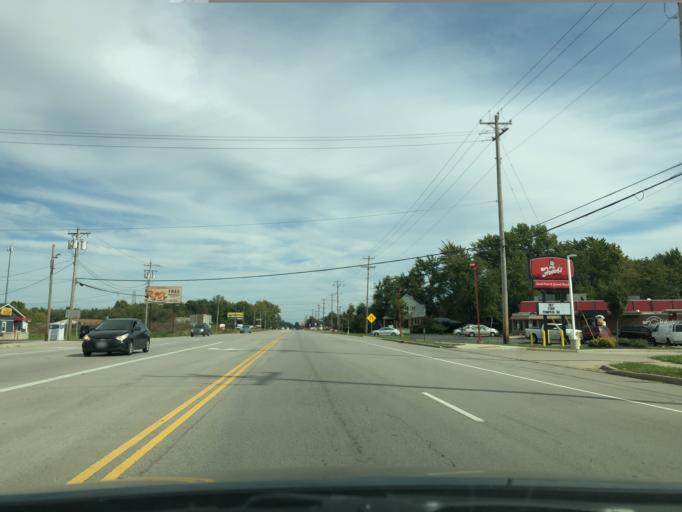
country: US
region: Ohio
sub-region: Clermont County
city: Mount Repose
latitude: 39.2028
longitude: -84.2210
